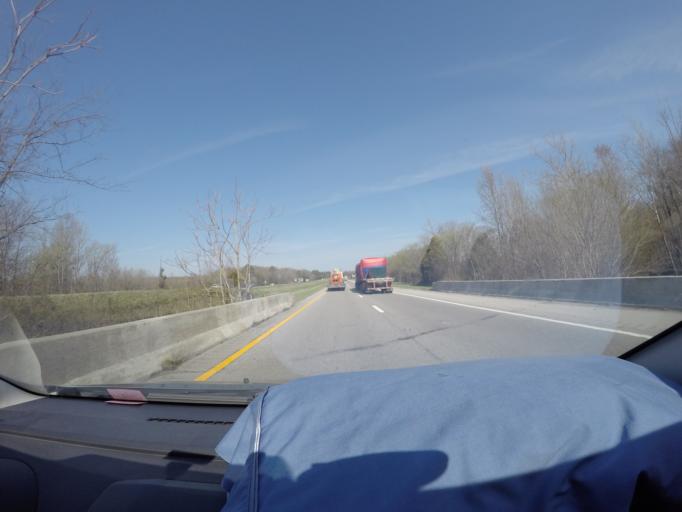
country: US
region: Tennessee
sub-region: Franklin County
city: Sewanee
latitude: 35.3542
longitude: -85.9523
